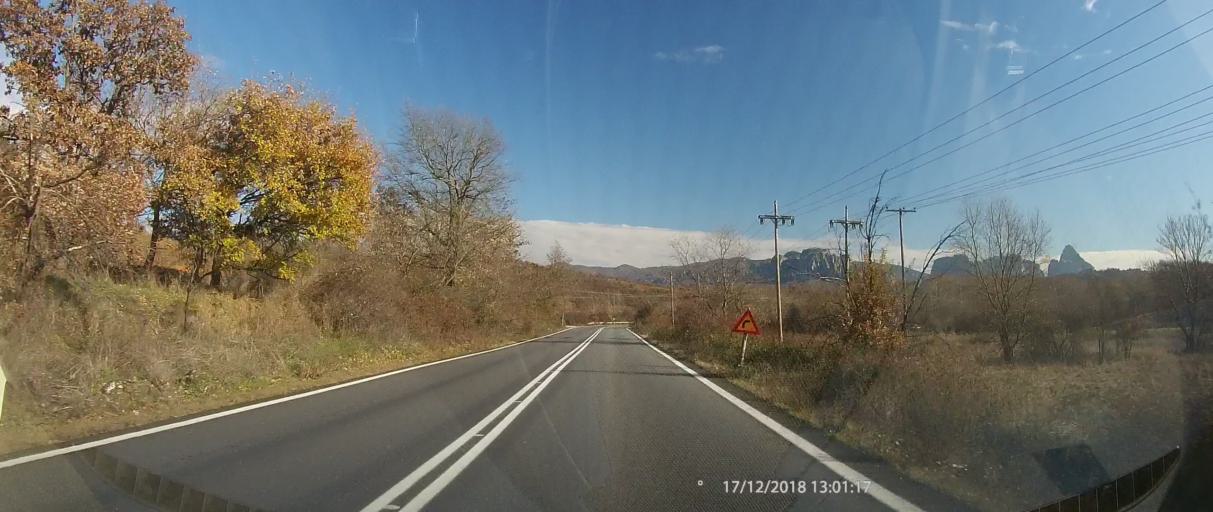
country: GR
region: Thessaly
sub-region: Trikala
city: Kastraki
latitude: 39.7324
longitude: 21.5800
